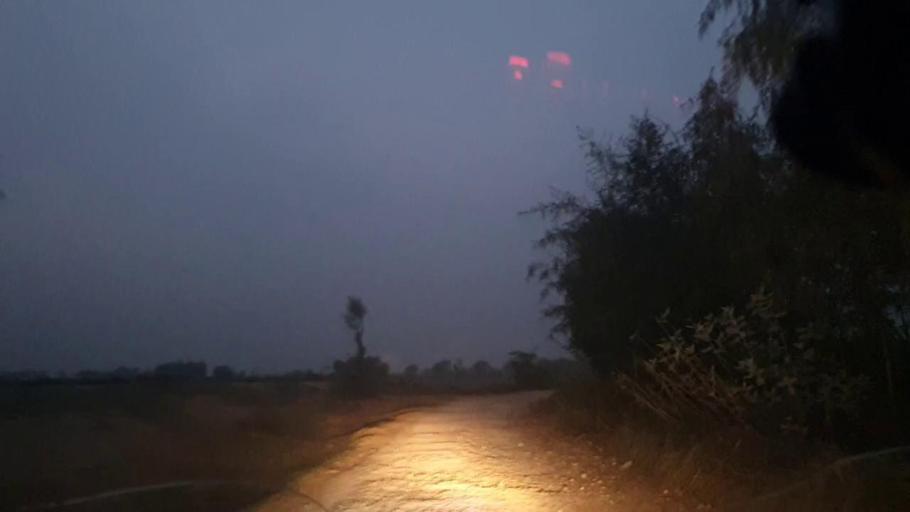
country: PK
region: Sindh
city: Hingorja
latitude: 27.2094
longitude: 68.3715
